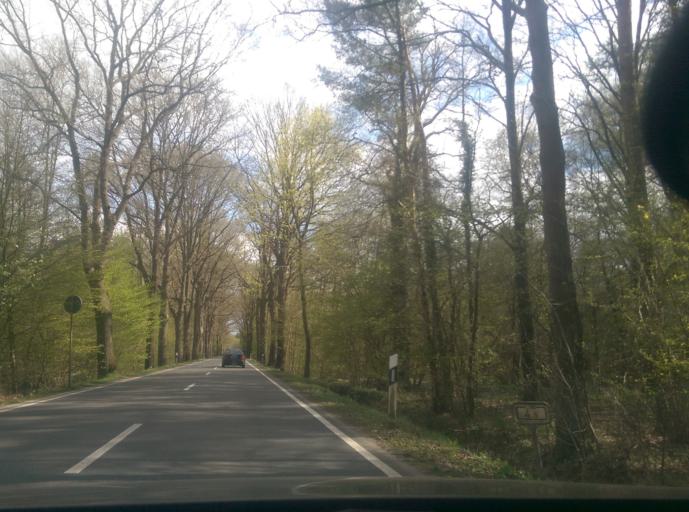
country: DE
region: Lower Saxony
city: Garbsen-Mitte
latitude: 52.5177
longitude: 9.6255
